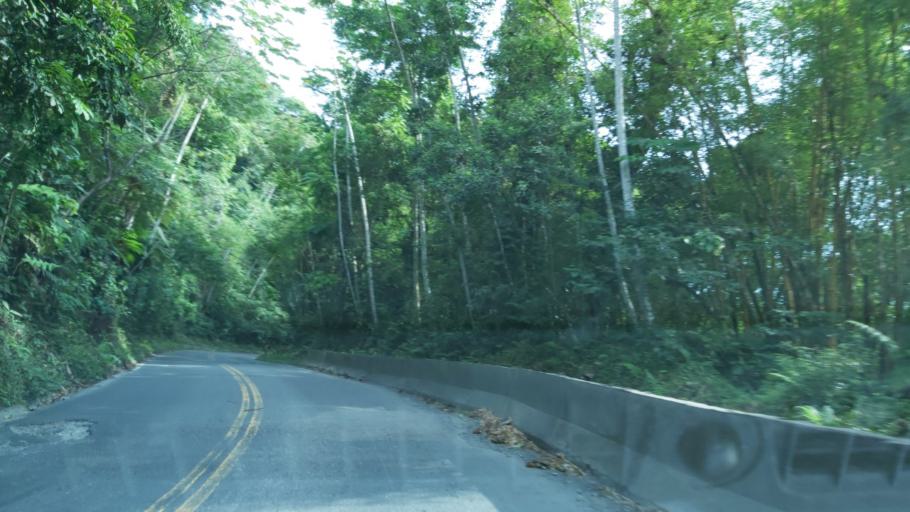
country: BR
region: Sao Paulo
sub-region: Juquia
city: Juquia
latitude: -24.1100
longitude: -47.6266
